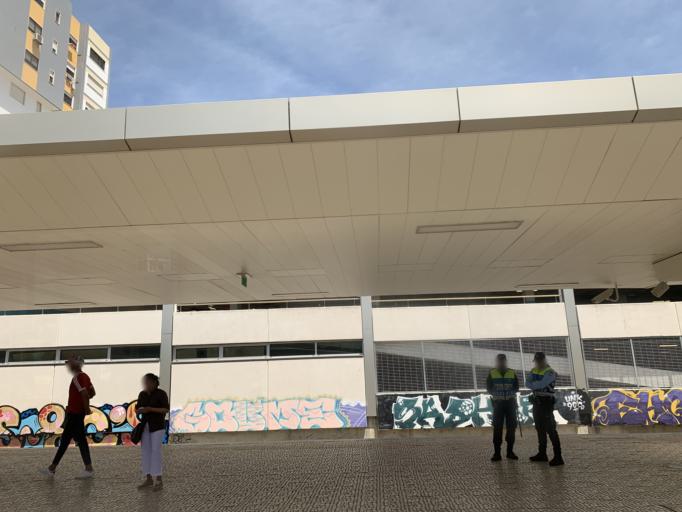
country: PT
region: Lisbon
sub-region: Oeiras
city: Barcarena
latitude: 38.7518
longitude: -9.2842
